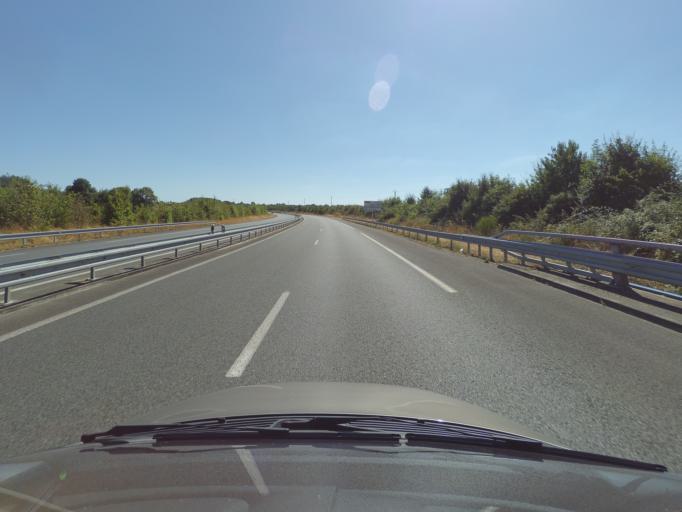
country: FR
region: Pays de la Loire
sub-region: Departement de Maine-et-Loire
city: Vezins
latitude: 47.1249
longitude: -0.7246
